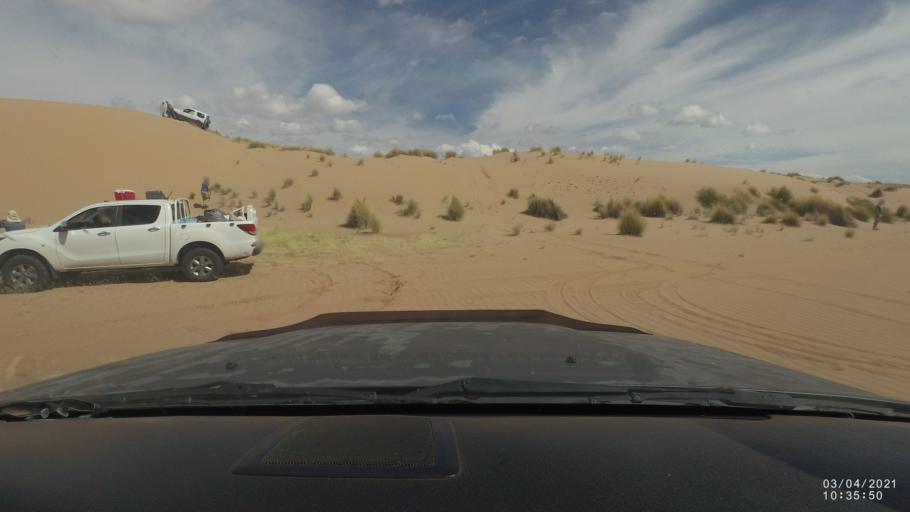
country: BO
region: Oruro
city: Poopo
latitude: -18.7051
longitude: -67.5212
